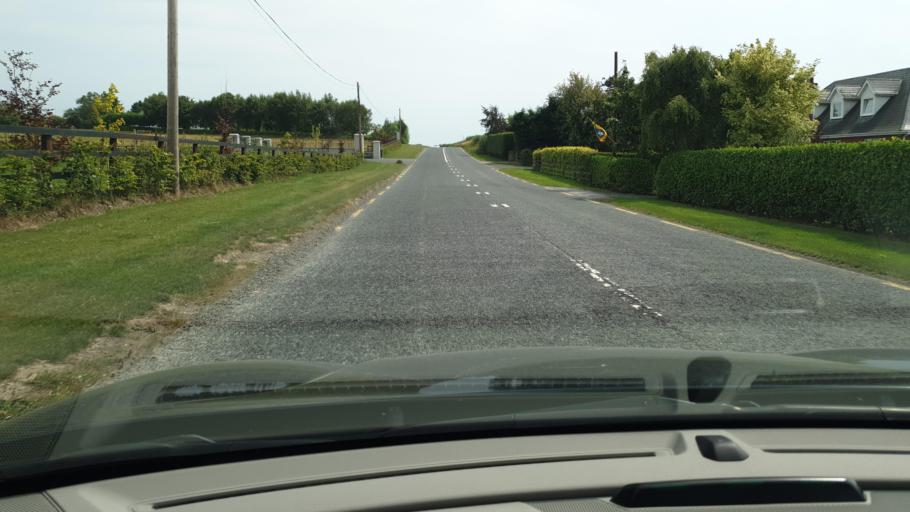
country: IE
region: Leinster
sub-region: An Mhi
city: Navan
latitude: 53.6387
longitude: -6.6110
